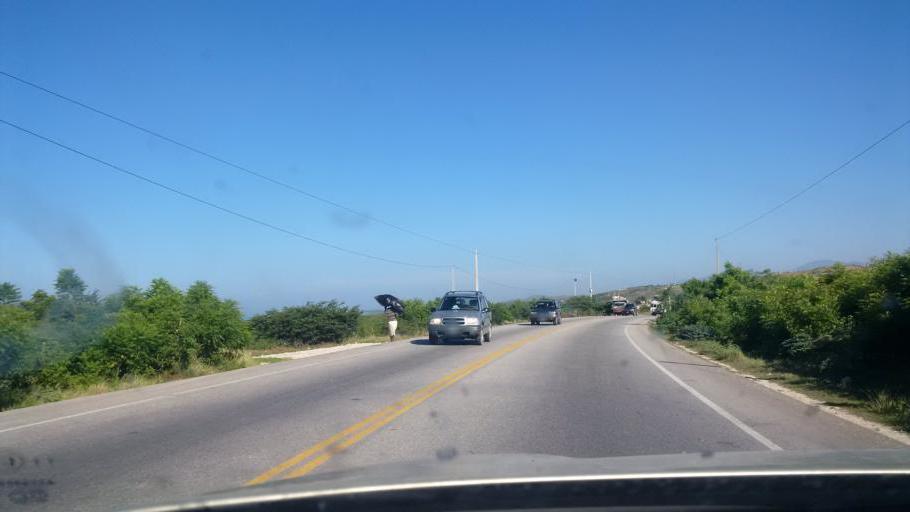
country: HT
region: Ouest
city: Cabaret
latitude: 18.6720
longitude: -72.3103
